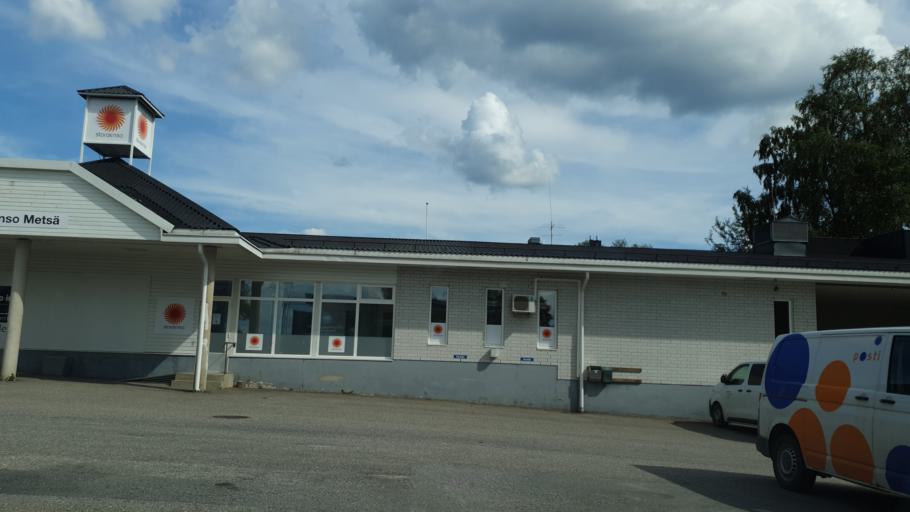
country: FI
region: Kainuu
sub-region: Kajaani
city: Sotkamo
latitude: 64.1301
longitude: 28.3812
